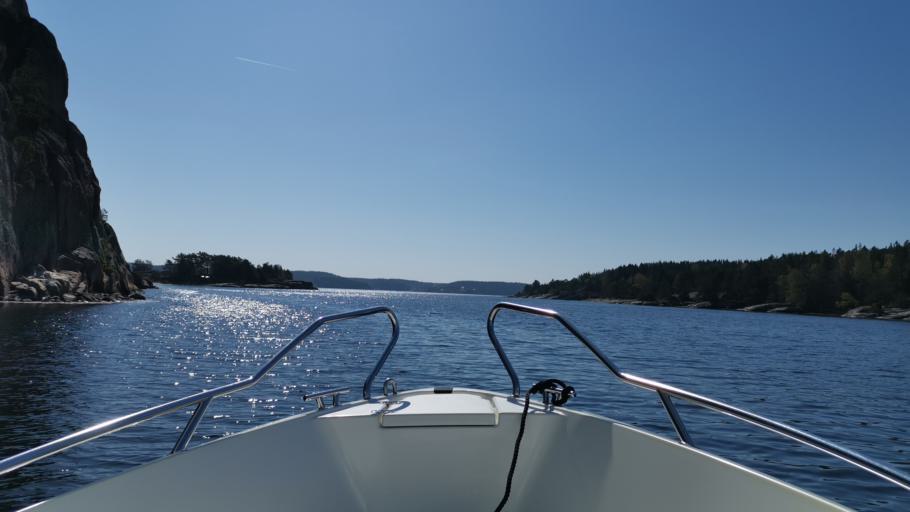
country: SE
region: Vaestra Goetaland
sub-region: Orust
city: Henan
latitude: 58.2545
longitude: 11.5739
